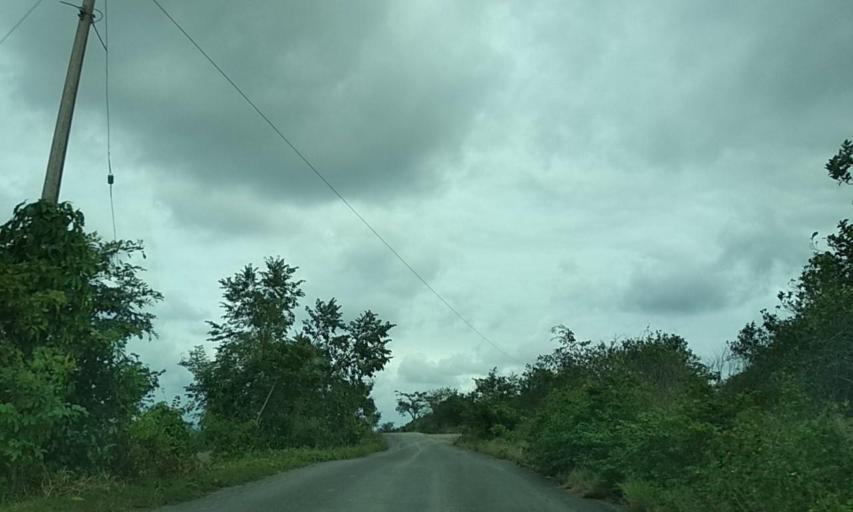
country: MX
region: Puebla
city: Espinal
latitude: 20.3307
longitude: -97.4062
